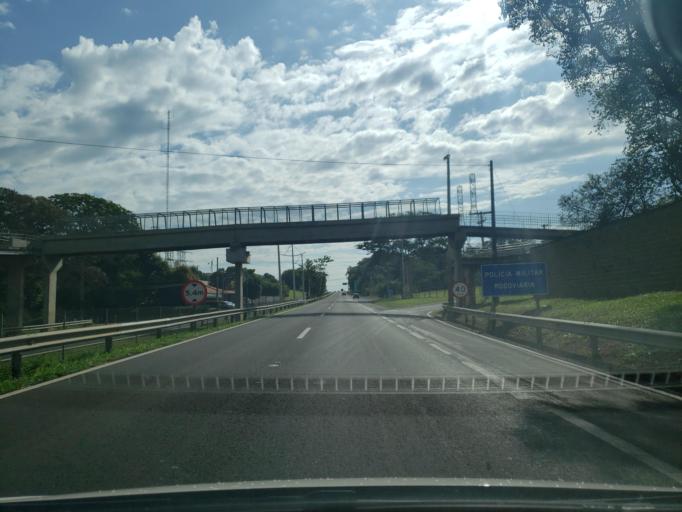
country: BR
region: Sao Paulo
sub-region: Lins
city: Lins
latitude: -21.6862
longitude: -49.7618
